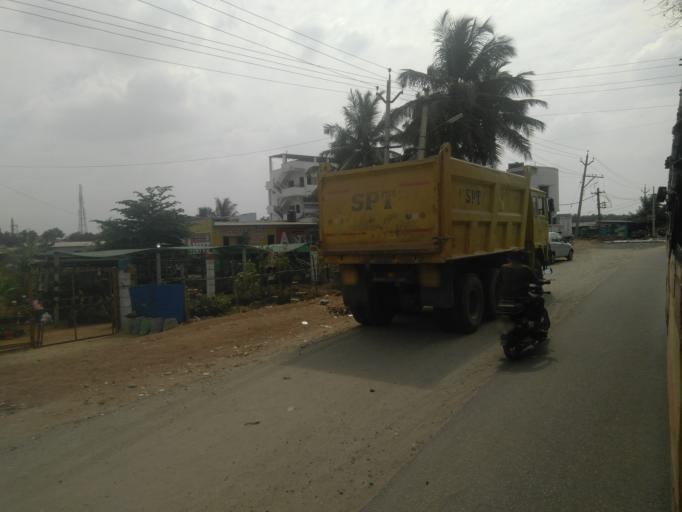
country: IN
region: Tamil Nadu
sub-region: Coimbatore
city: Irugur
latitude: 11.0183
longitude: 77.0945
